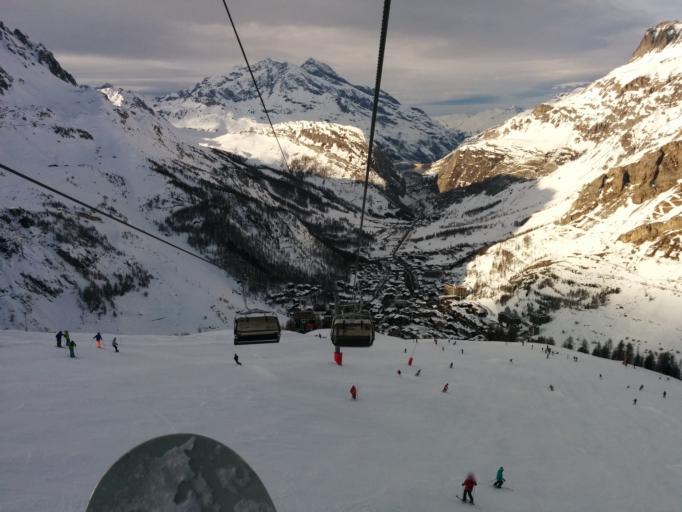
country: FR
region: Rhone-Alpes
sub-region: Departement de la Savoie
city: Val-d'Isere
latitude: 45.4386
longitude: 6.9879
